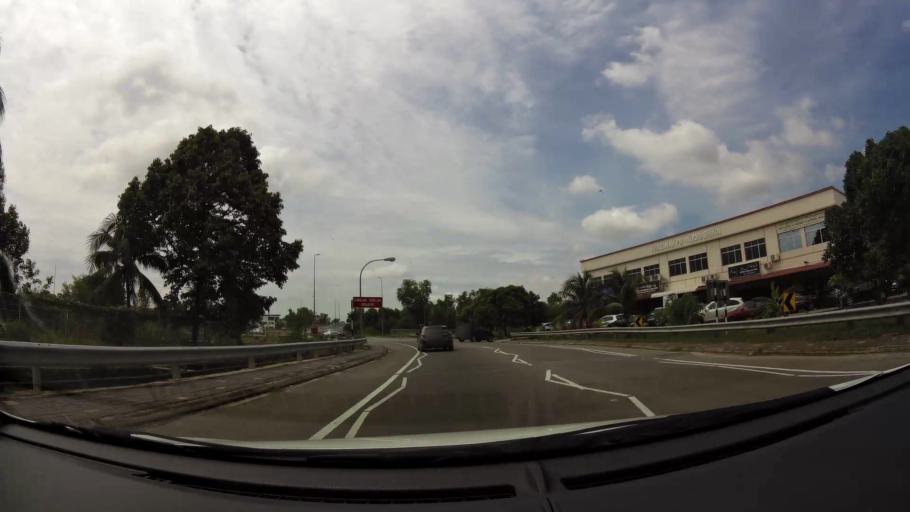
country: BN
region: Brunei and Muara
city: Bandar Seri Begawan
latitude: 4.9142
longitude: 114.9248
